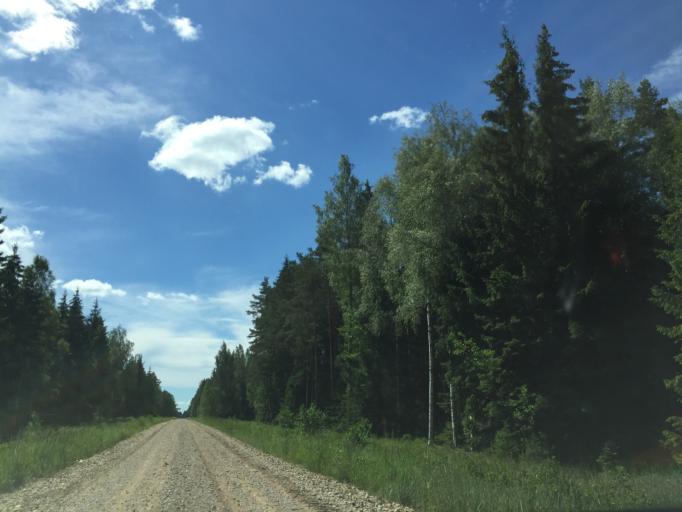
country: LV
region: Ventspils Rajons
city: Piltene
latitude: 57.2689
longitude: 21.8348
